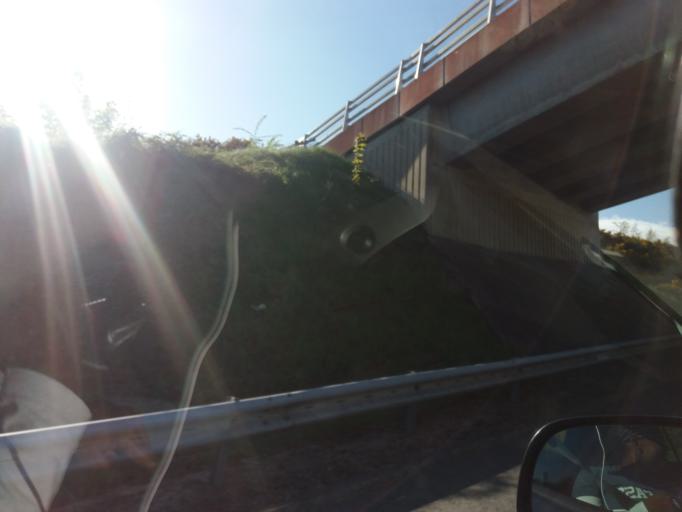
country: IE
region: Munster
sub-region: Waterford
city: Waterford
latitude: 52.3411
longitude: -7.1637
